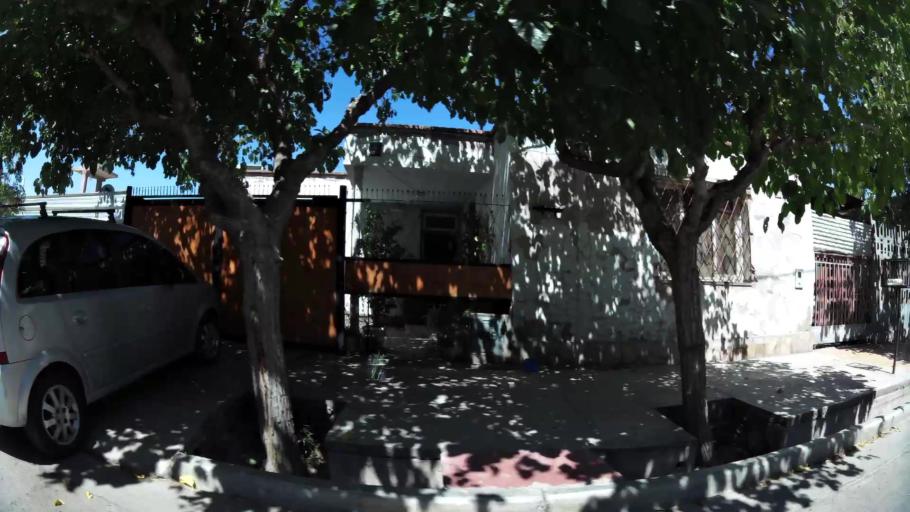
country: AR
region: San Juan
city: San Juan
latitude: -31.5165
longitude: -68.5212
